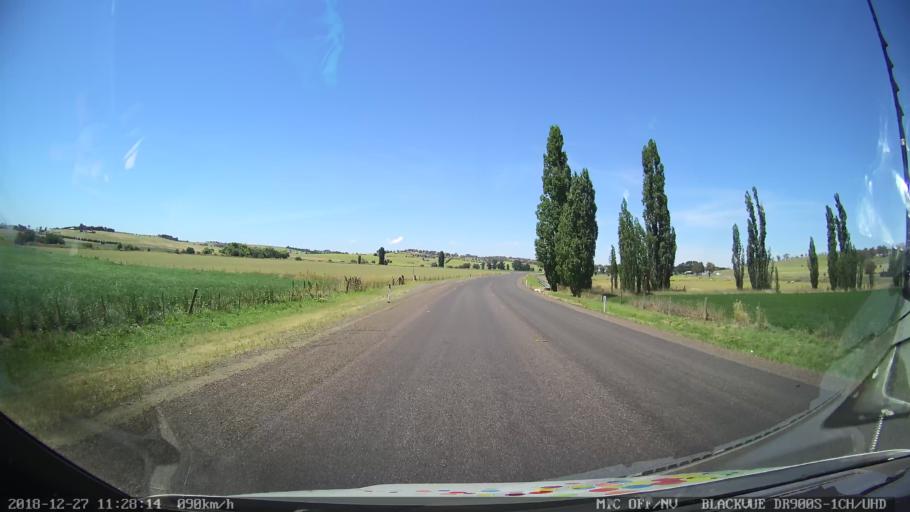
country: AU
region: New South Wales
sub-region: Bathurst Regional
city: Perthville
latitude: -33.4732
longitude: 149.5647
